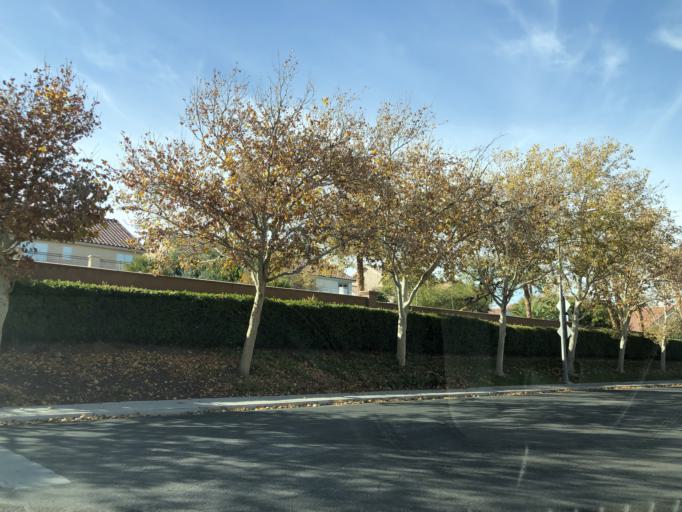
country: US
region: Nevada
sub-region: Clark County
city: Whitney
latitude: 36.0156
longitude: -115.0799
